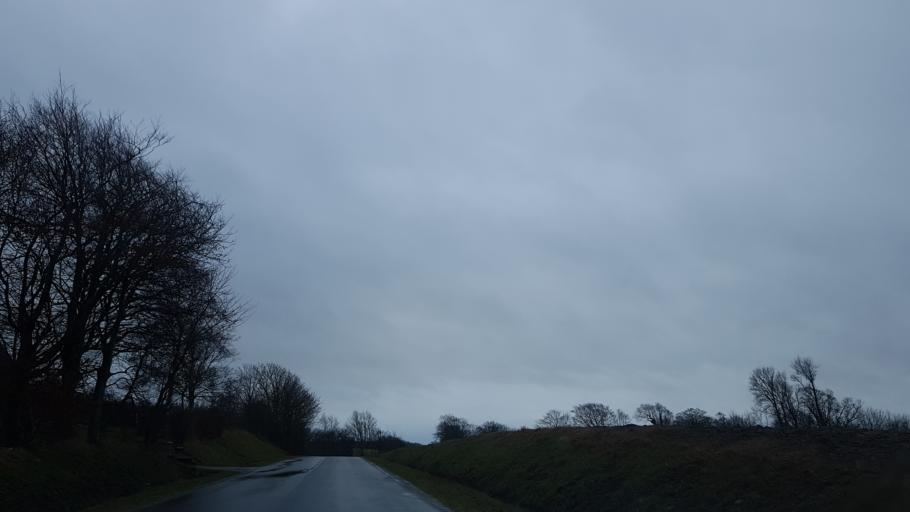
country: DK
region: South Denmark
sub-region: Kolding Kommune
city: Vamdrup
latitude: 55.3811
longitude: 9.2954
